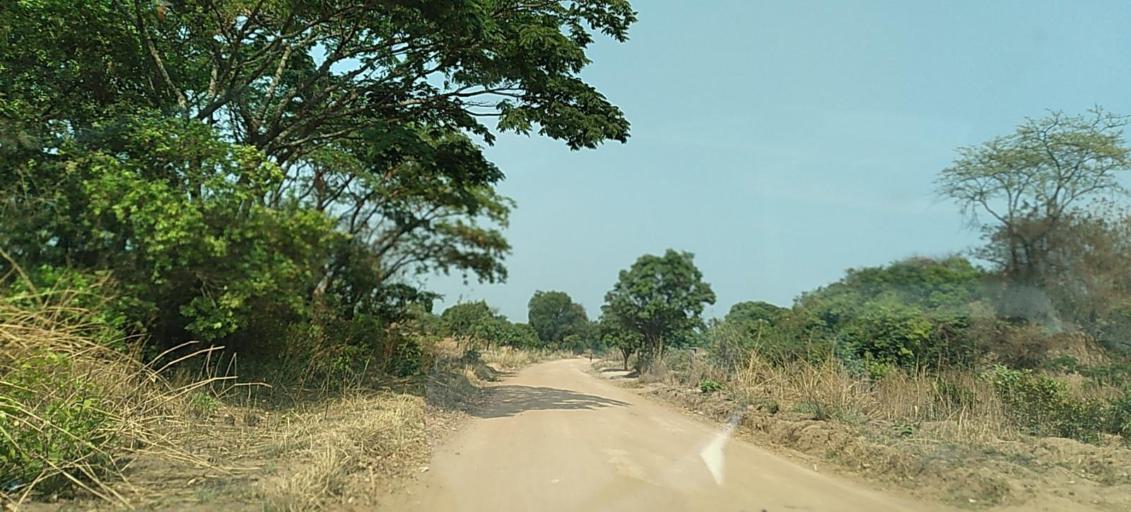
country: ZM
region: Copperbelt
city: Chililabombwe
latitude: -12.3366
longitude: 27.7258
